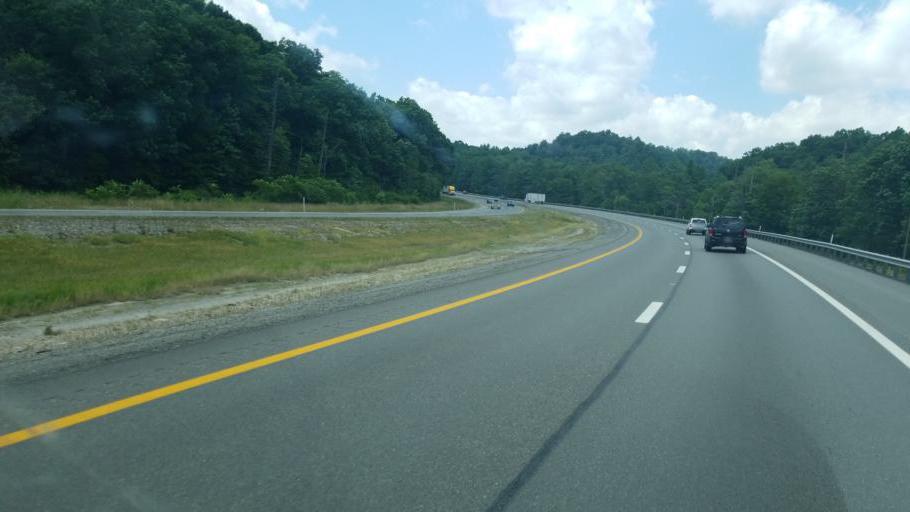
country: US
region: West Virginia
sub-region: Raleigh County
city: Beaver
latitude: 37.7173
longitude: -81.1538
